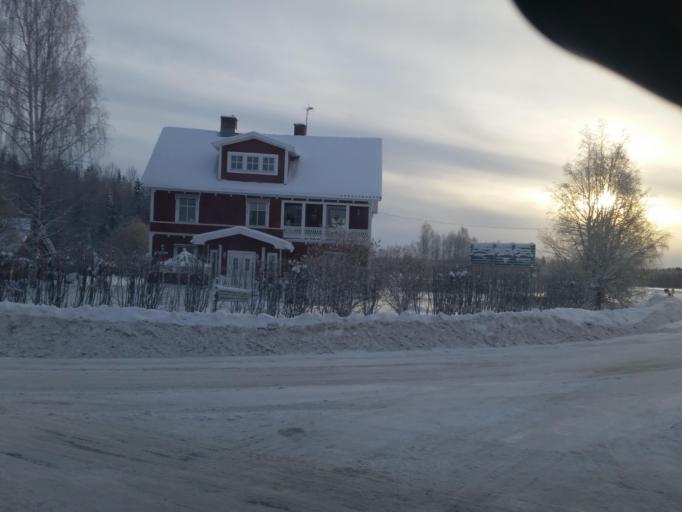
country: SE
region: Norrbotten
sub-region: Pitea Kommun
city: Norrfjarden
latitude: 65.5166
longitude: 21.4950
